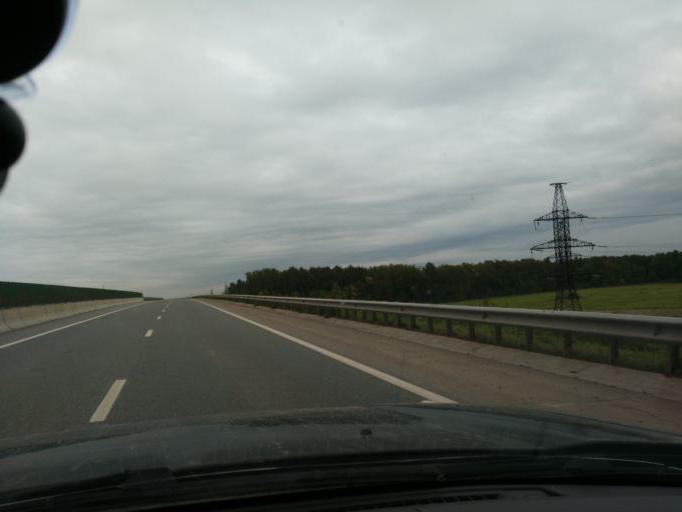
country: RU
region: Perm
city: Froly
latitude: 57.9314
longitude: 56.2908
